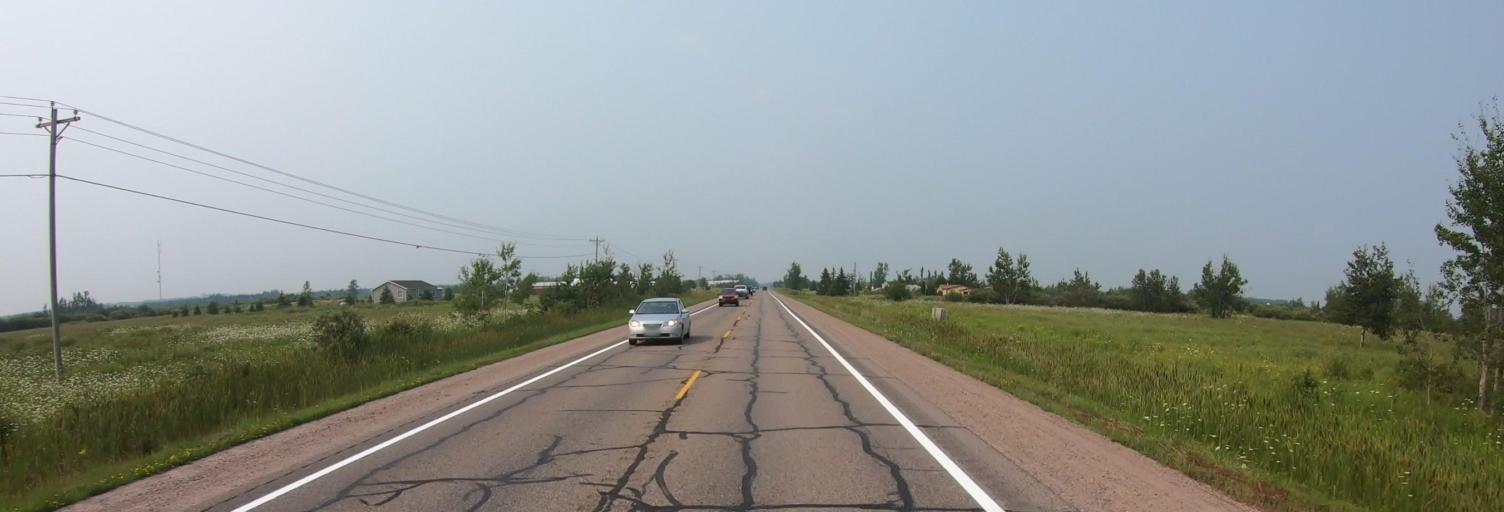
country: US
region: Michigan
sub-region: Chippewa County
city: Sault Ste. Marie
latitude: 46.4293
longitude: -84.3535
